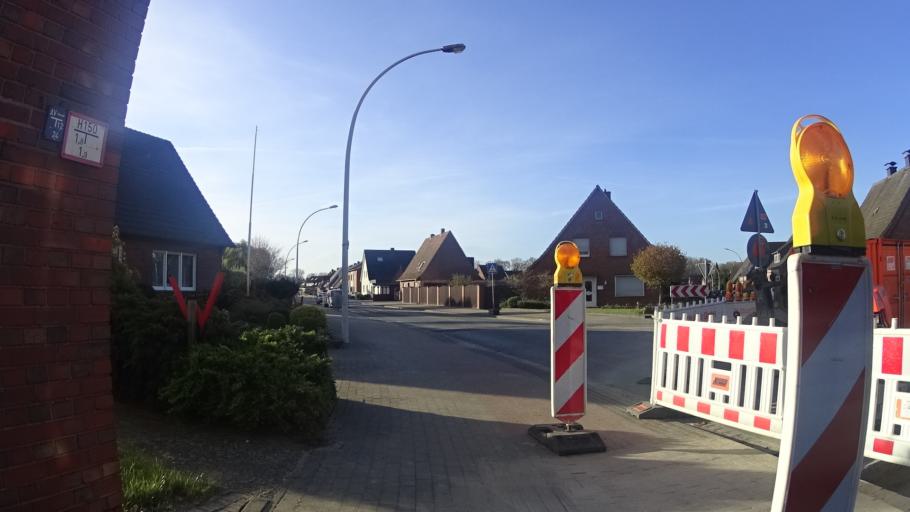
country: DE
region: North Rhine-Westphalia
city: Emsdetten
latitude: 52.1545
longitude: 7.5284
